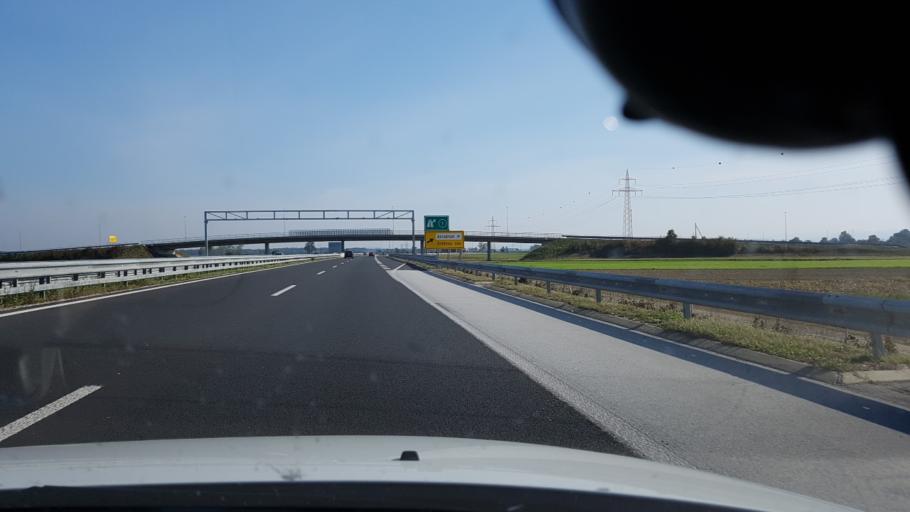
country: SI
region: Hoce-Slivnica
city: Hotinja Vas
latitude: 46.4759
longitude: 15.6722
